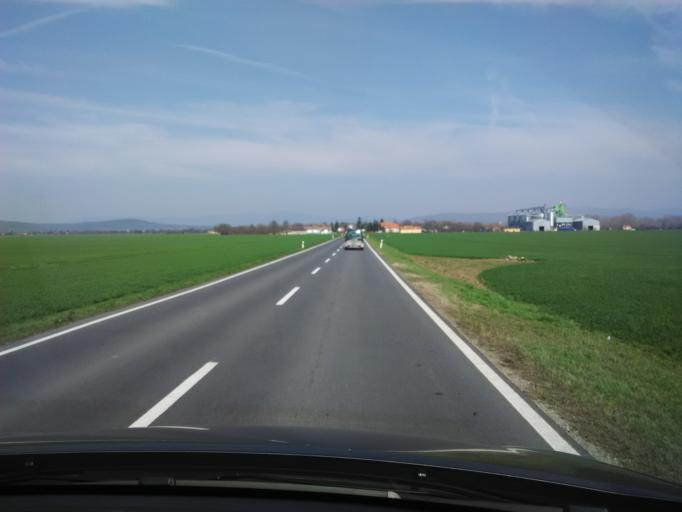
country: SK
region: Nitriansky
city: Tlmace
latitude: 48.2273
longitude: 18.5199
